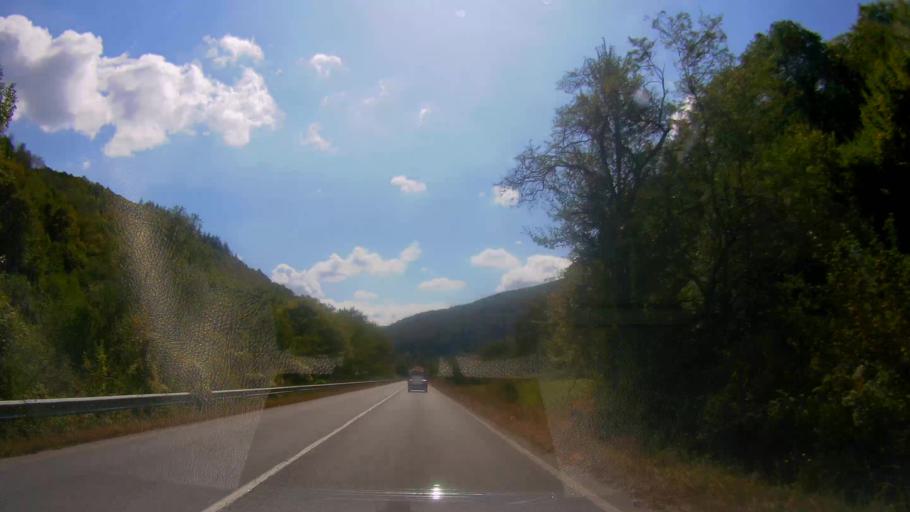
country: BG
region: Stara Zagora
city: Gurkovo
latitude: 42.7439
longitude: 25.7092
